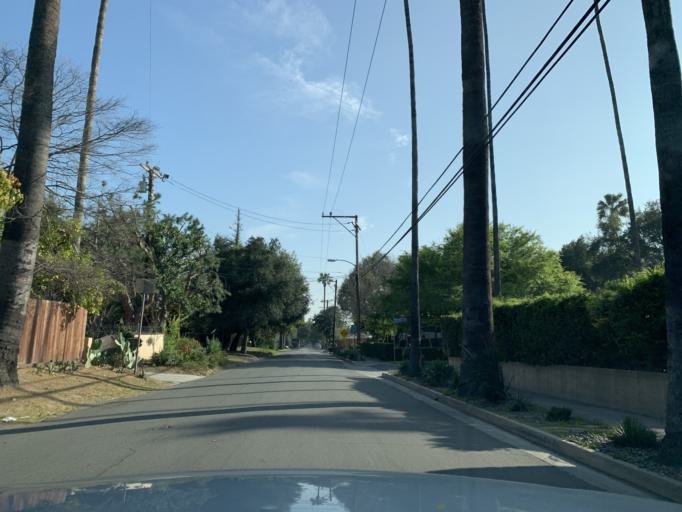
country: US
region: California
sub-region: Los Angeles County
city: Altadena
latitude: 34.1769
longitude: -118.1232
